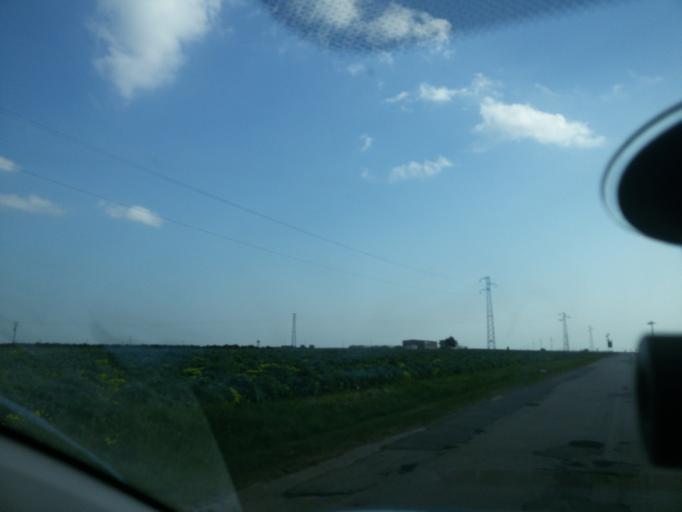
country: IT
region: Apulia
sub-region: Provincia di Brindisi
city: Mesagne
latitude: 40.6439
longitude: 17.8154
